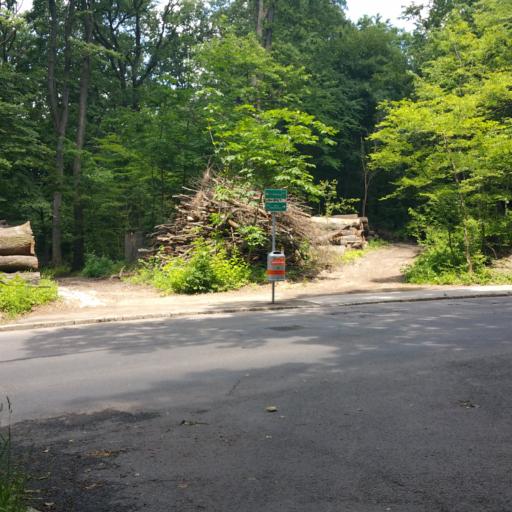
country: AT
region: Vienna
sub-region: Wien Stadt
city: Vienna
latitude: 48.2168
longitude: 16.2780
